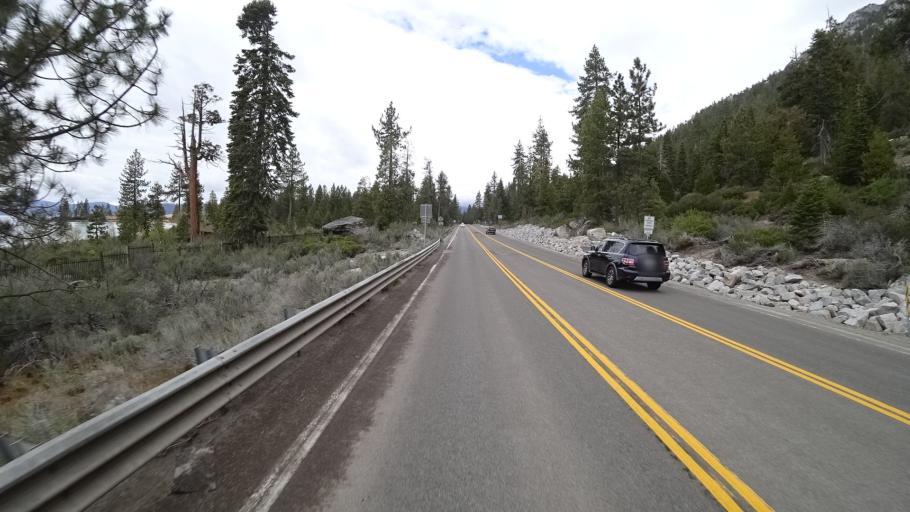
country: US
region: Nevada
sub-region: Washoe County
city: Incline Village
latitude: 39.1949
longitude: -119.9270
